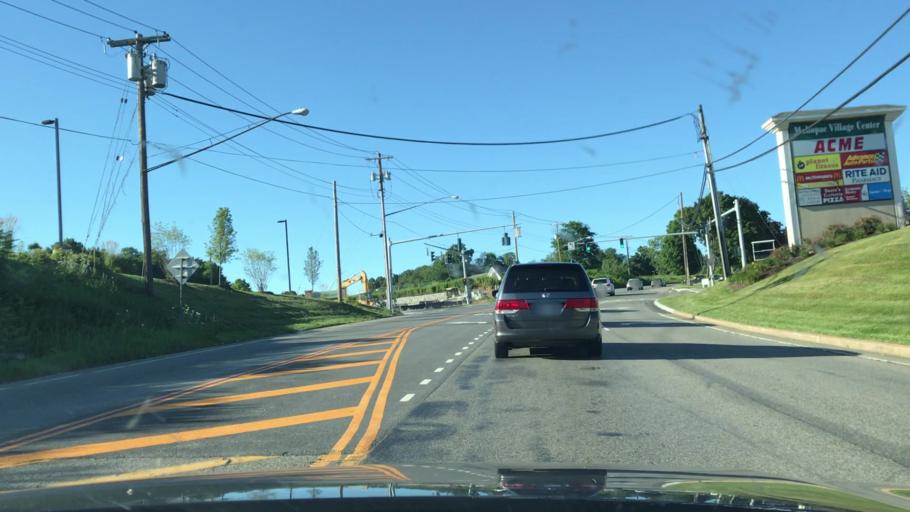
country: US
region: New York
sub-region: Westchester County
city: Shenorock
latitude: 41.3477
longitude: -73.7562
